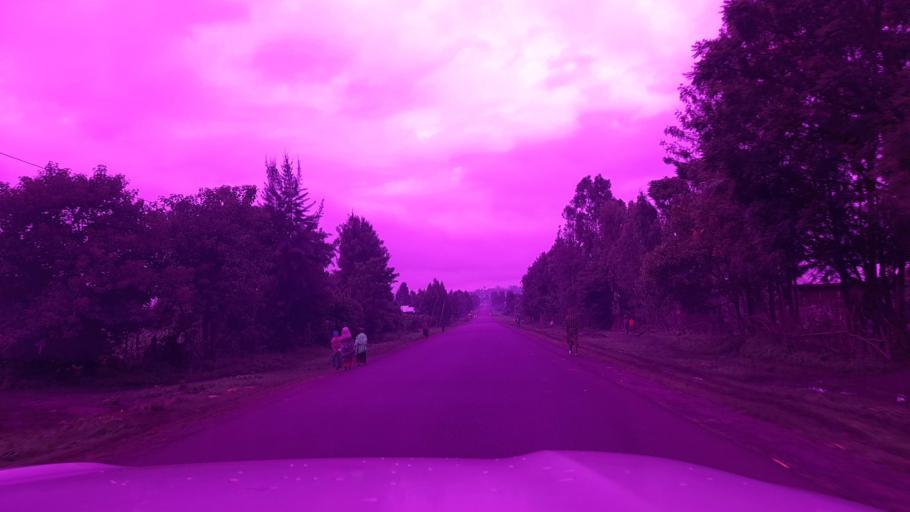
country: ET
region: Oromiya
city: Waliso
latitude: 8.2804
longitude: 37.6913
